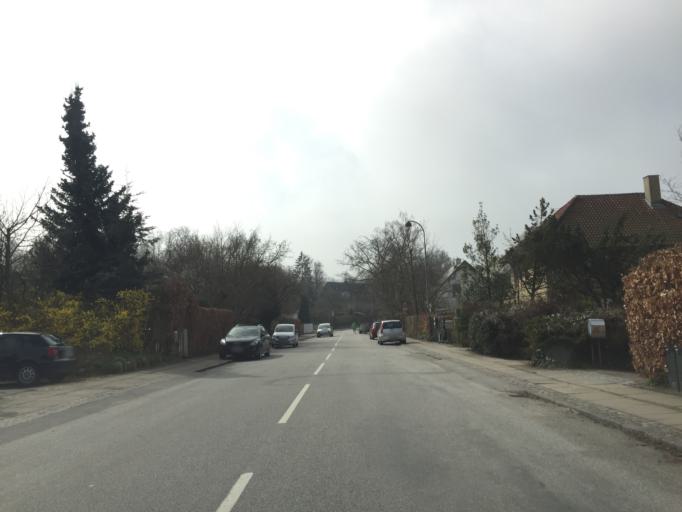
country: DK
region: Capital Region
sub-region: Lyngby-Tarbaek Kommune
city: Kongens Lyngby
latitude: 55.7632
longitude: 12.5460
